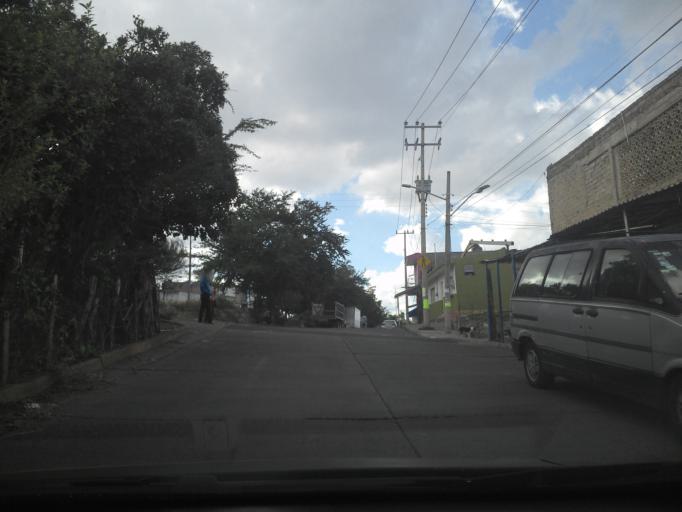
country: MX
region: Jalisco
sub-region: Tlajomulco de Zuniga
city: Altus Bosques
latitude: 20.6164
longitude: -103.3706
